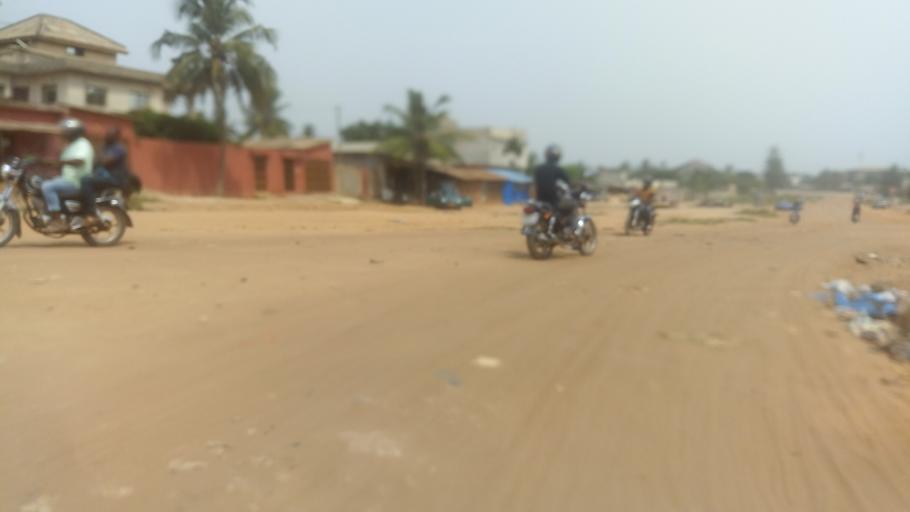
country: TG
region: Maritime
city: Lome
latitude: 6.1840
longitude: 1.1710
